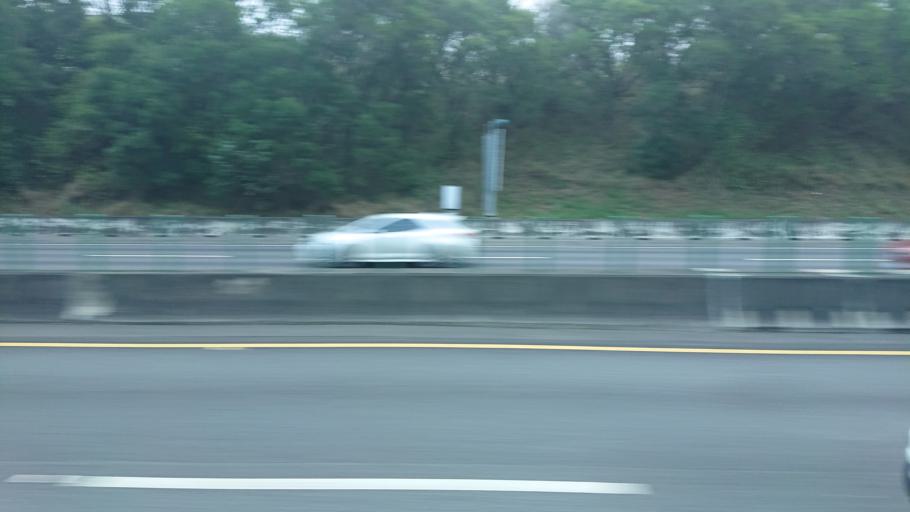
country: TW
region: Taiwan
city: Fengyuan
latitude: 24.2892
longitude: 120.6950
